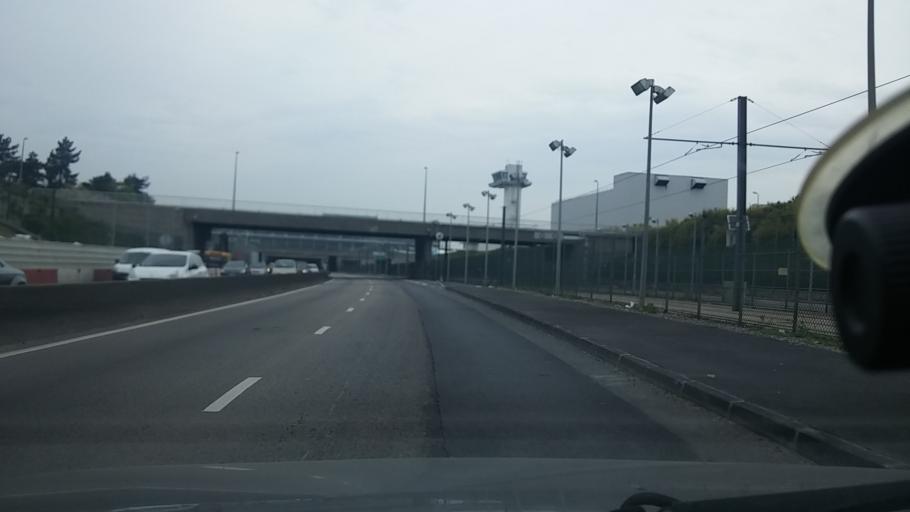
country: FR
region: Ile-de-France
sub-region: Departement de l'Essonne
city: Paray-Vieille-Poste
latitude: 48.7212
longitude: 2.3708
